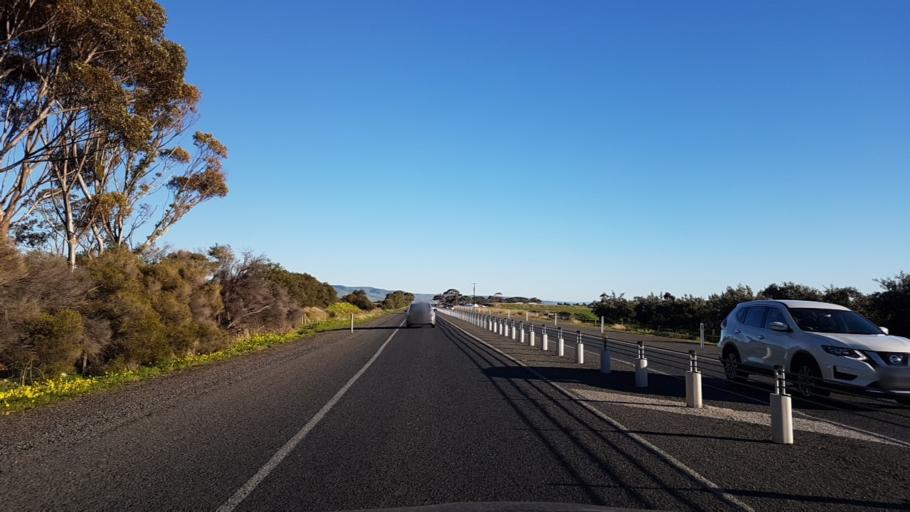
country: AU
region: South Australia
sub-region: Onkaparinga
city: Aldinga
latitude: -35.2555
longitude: 138.4936
